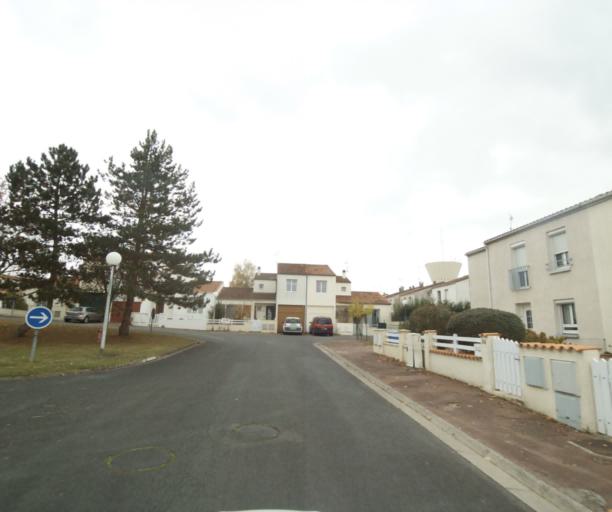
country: FR
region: Poitou-Charentes
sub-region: Departement de la Charente-Maritime
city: Saintes
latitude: 45.7334
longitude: -0.6518
